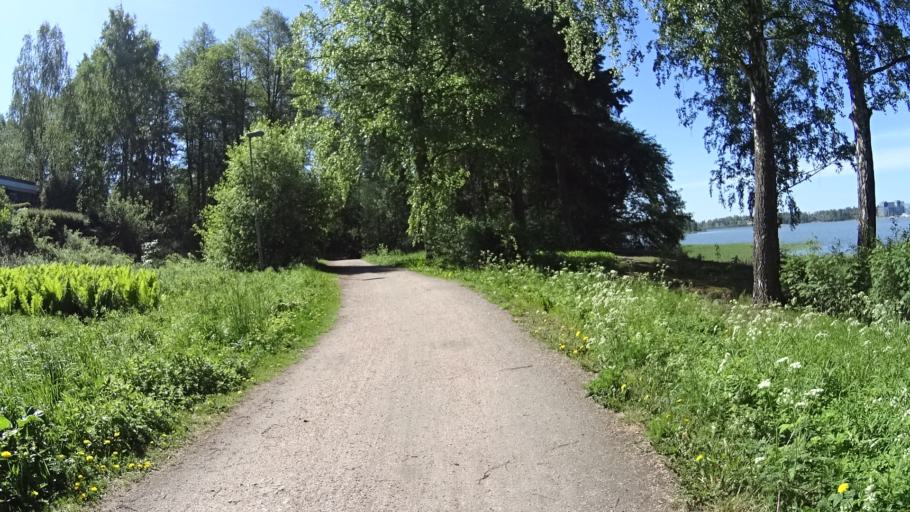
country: FI
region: Uusimaa
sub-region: Helsinki
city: Teekkarikylae
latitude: 60.1787
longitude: 24.8476
